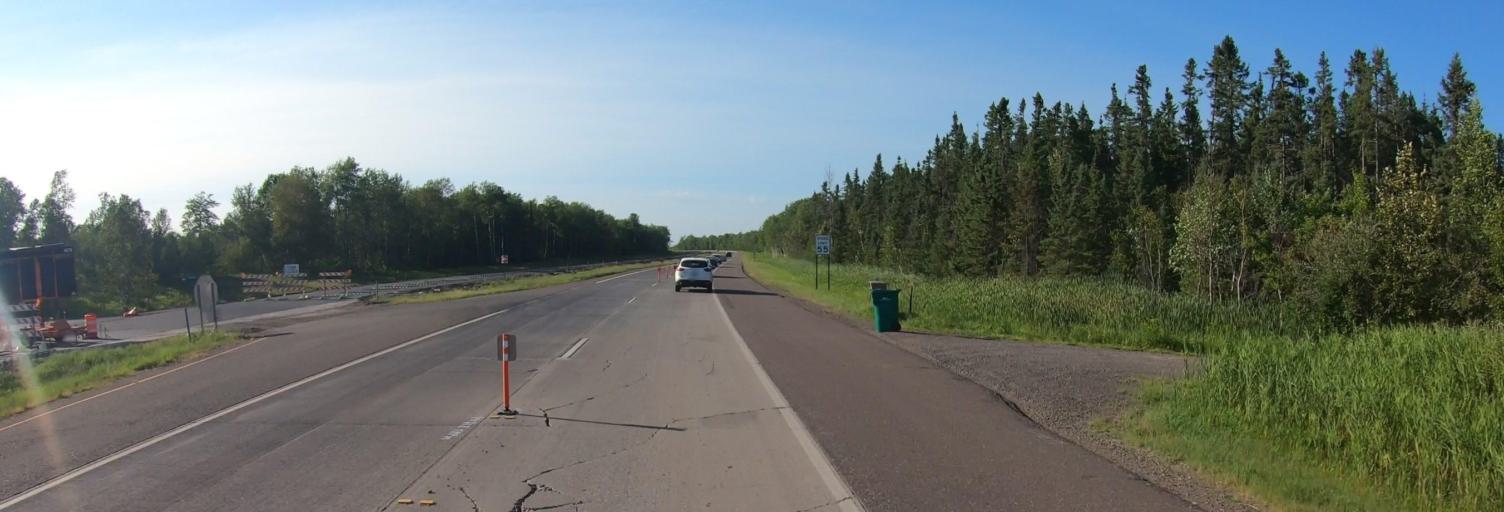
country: US
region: Minnesota
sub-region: Saint Louis County
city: Hermantown
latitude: 46.8832
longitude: -92.3522
